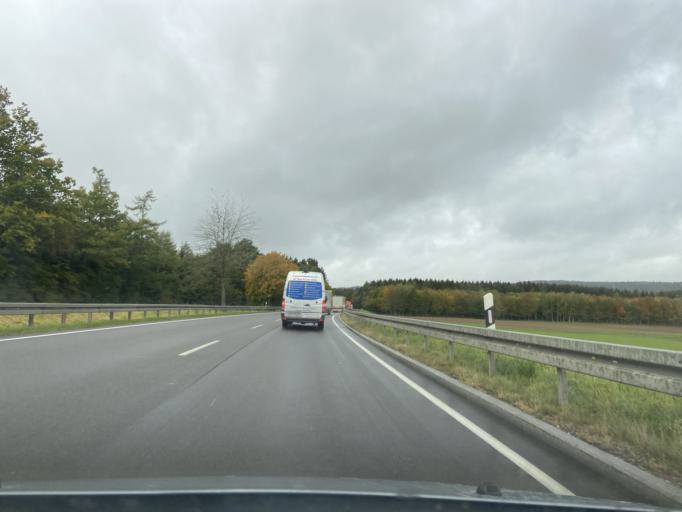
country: DE
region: Baden-Wuerttemberg
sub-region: Freiburg Region
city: Buchheim
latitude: 47.9862
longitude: 9.0260
